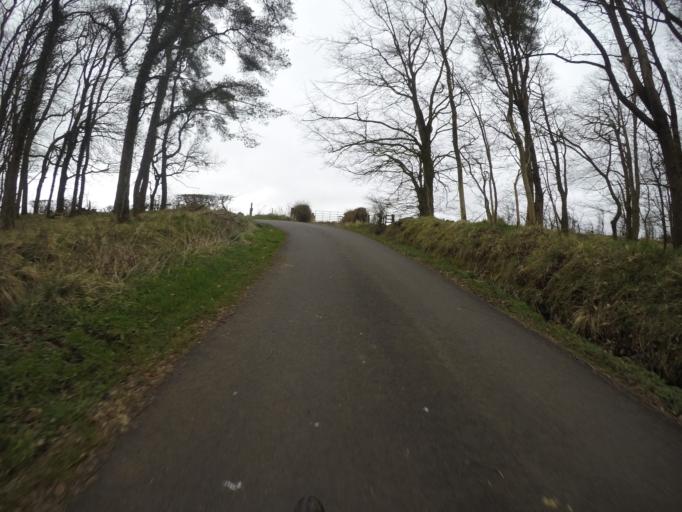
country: GB
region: Scotland
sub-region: East Ayrshire
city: Galston
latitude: 55.6240
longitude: -4.3562
